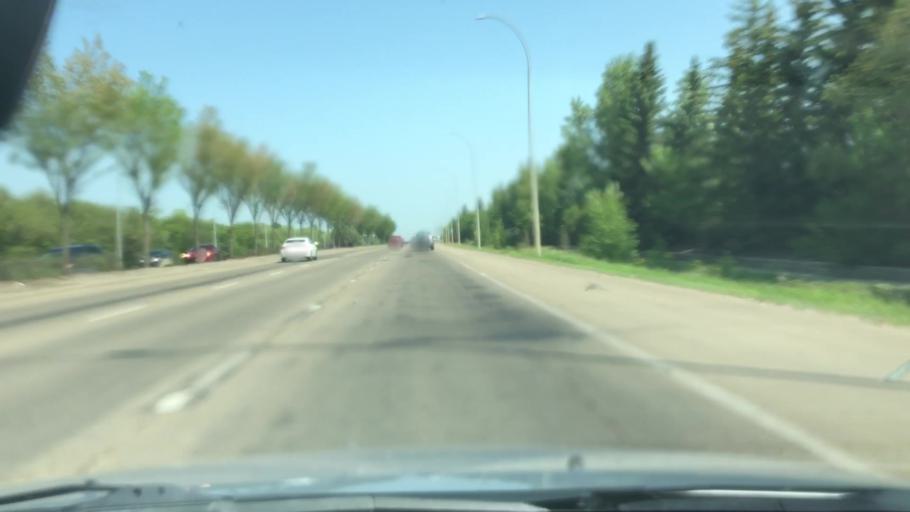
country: CA
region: Alberta
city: Edmonton
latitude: 53.6092
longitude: -113.4917
